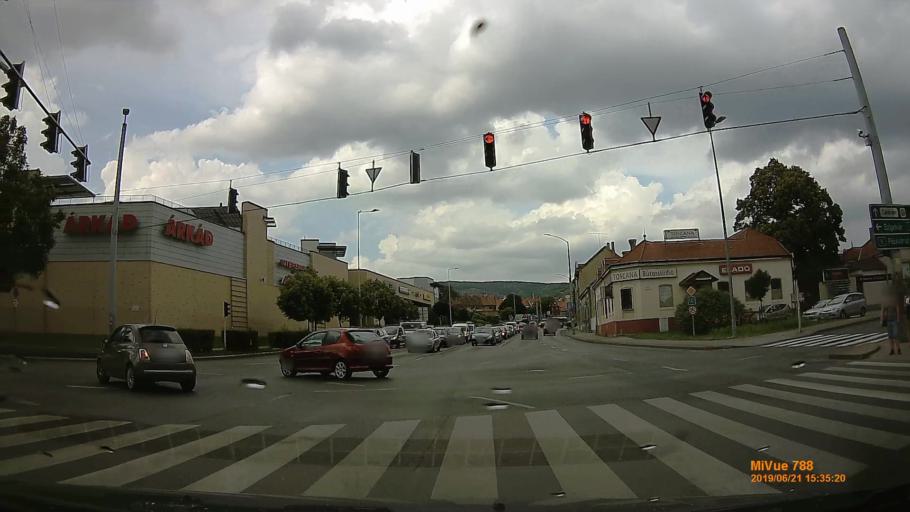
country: HU
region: Baranya
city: Pecs
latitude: 46.0710
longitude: 18.2326
